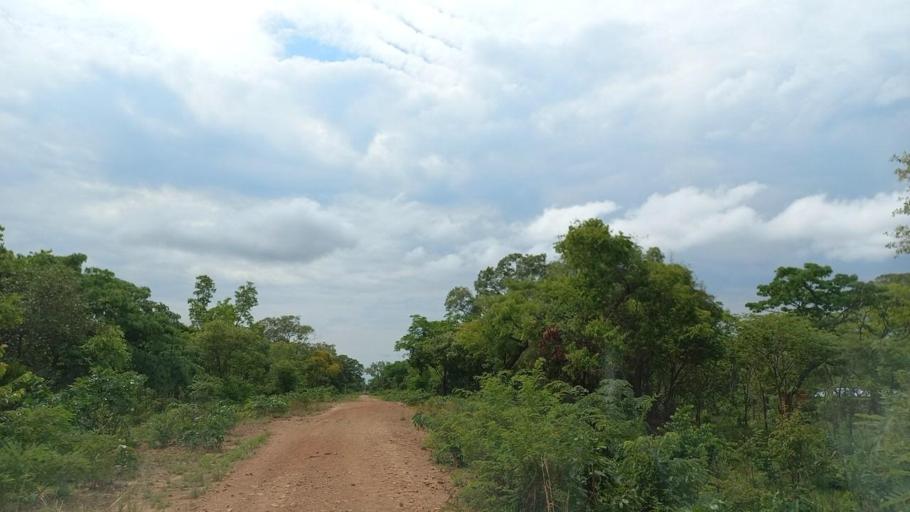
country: ZM
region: North-Western
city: Kalengwa
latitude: -13.4598
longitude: 25.0057
